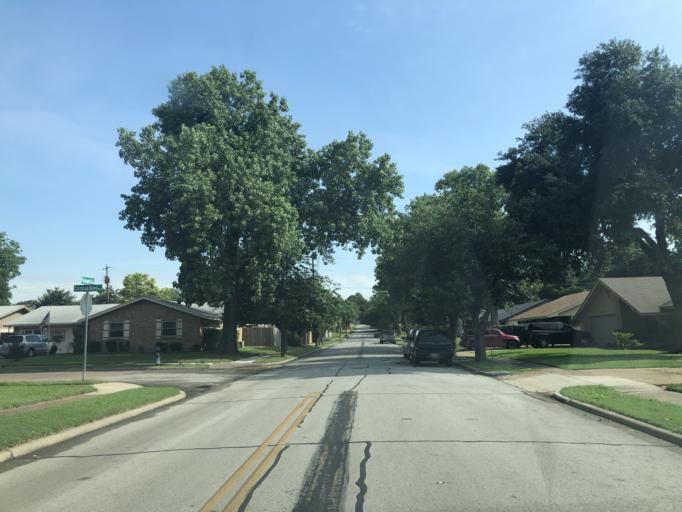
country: US
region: Texas
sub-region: Dallas County
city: Irving
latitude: 32.7971
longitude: -96.9689
